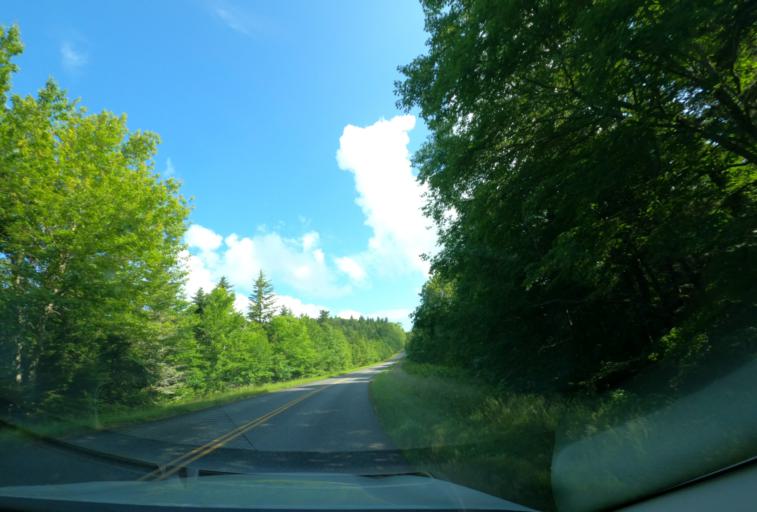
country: US
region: North Carolina
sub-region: Haywood County
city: Hazelwood
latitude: 35.3395
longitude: -82.9707
